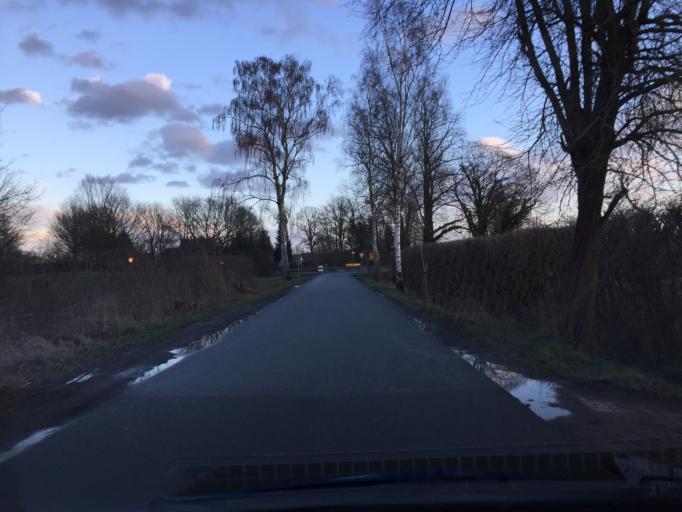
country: DE
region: Lower Saxony
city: Ludersburg
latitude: 53.3236
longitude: 10.5751
